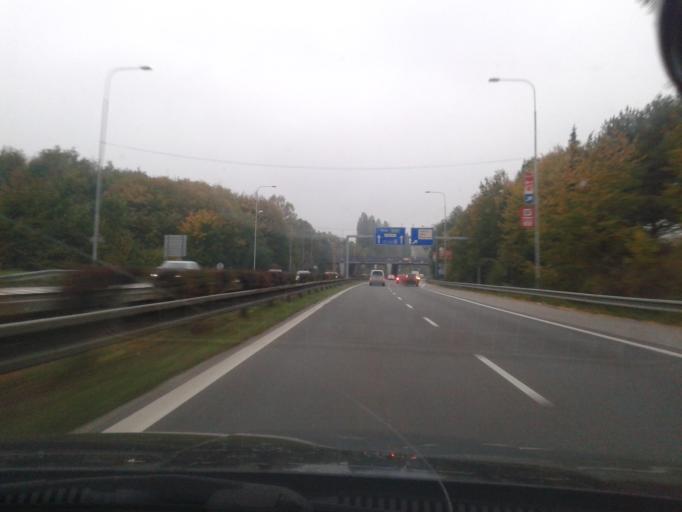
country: CZ
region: Moravskoslezsky
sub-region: Okres Ostrava-Mesto
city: Ostrava
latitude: 49.7973
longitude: 18.2362
